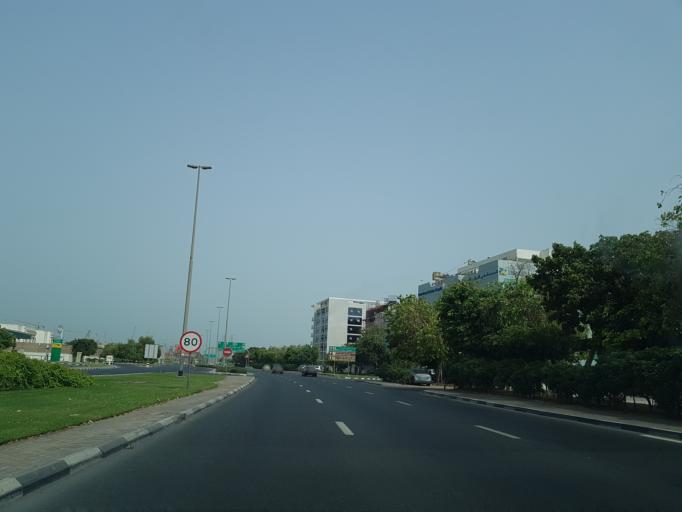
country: AE
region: Ash Shariqah
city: Sharjah
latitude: 25.2477
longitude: 55.2839
